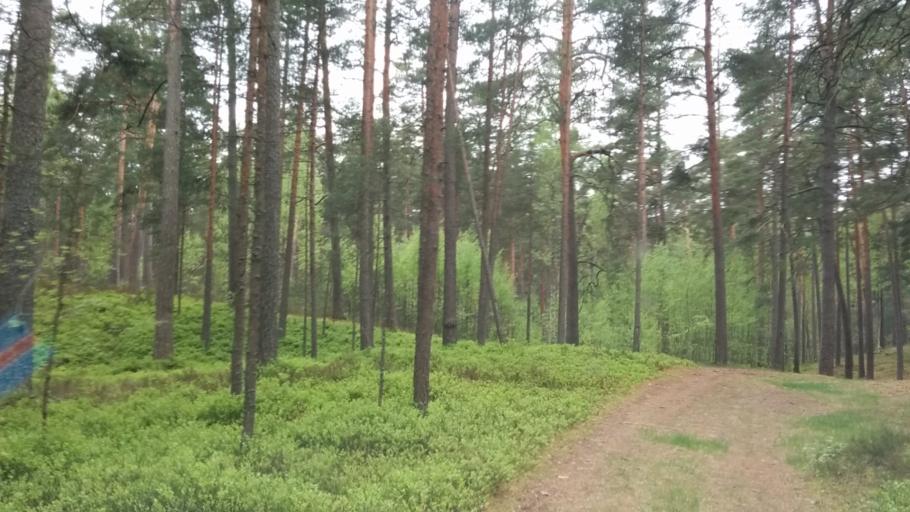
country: LV
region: Babite
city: Pinki
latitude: 56.9356
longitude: 23.9282
